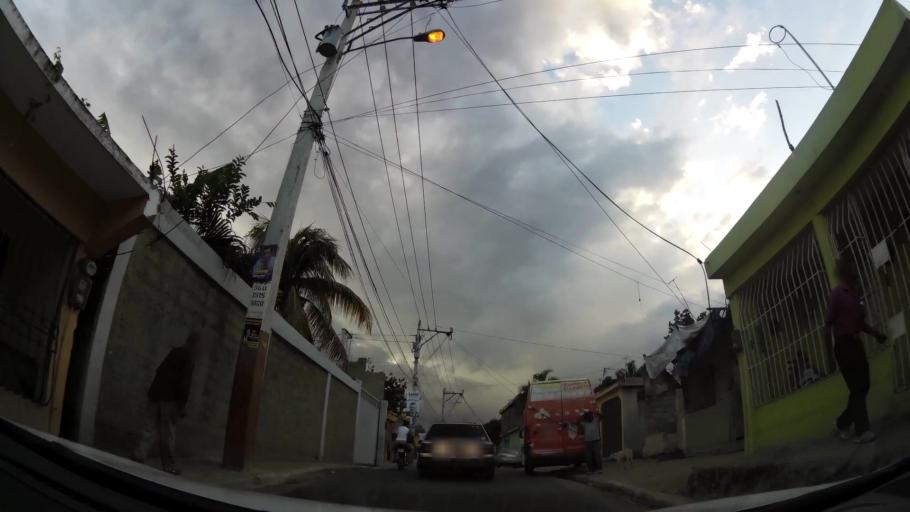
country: DO
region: Santo Domingo
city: Santo Domingo Oeste
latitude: 18.5246
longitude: -70.0175
